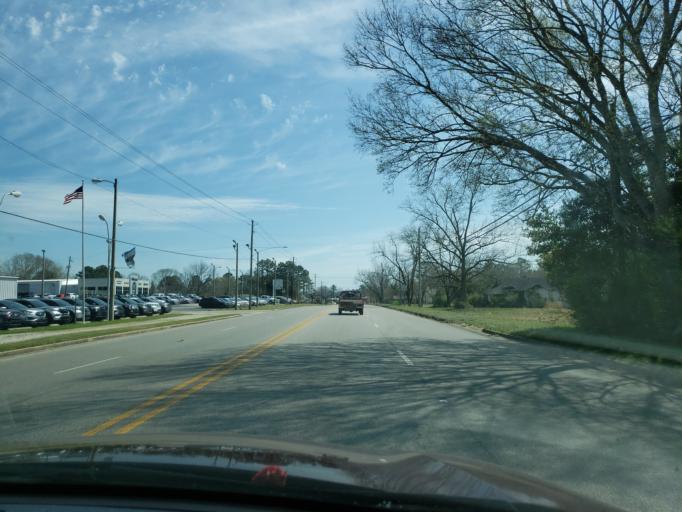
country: US
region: Alabama
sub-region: Elmore County
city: Tallassee
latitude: 32.5577
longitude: -85.9269
